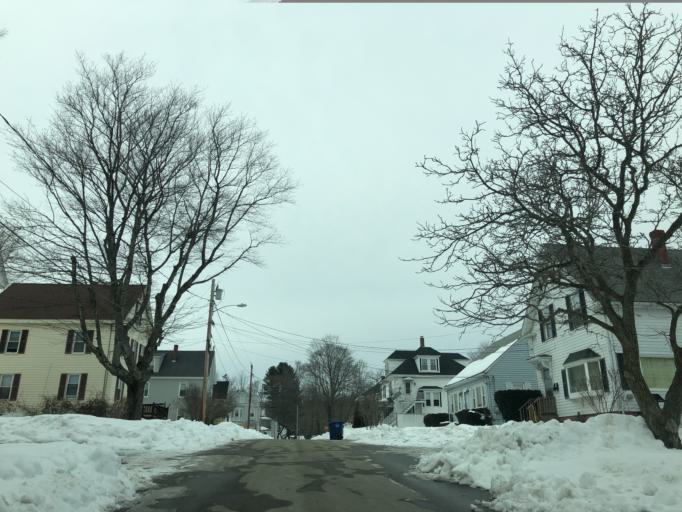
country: US
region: Maine
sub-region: Cumberland County
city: Westbrook
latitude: 43.6804
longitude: -70.3591
